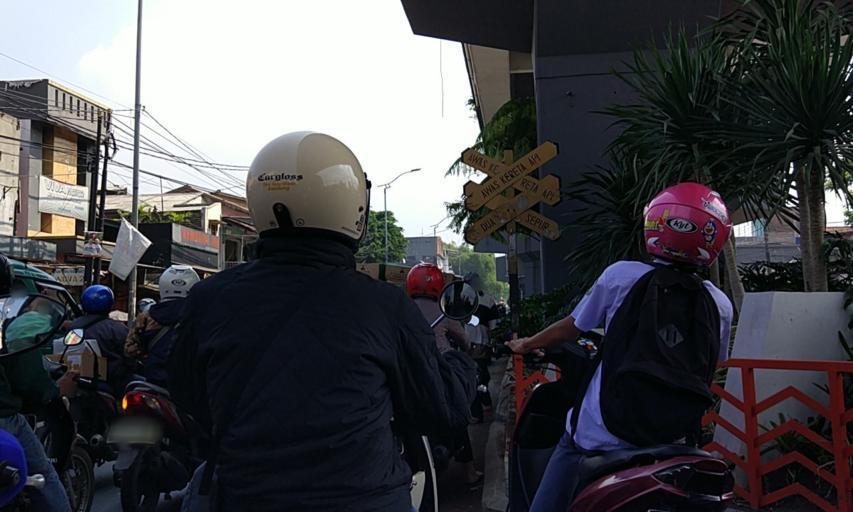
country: ID
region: West Java
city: Cimahi
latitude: -6.8958
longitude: 107.5601
